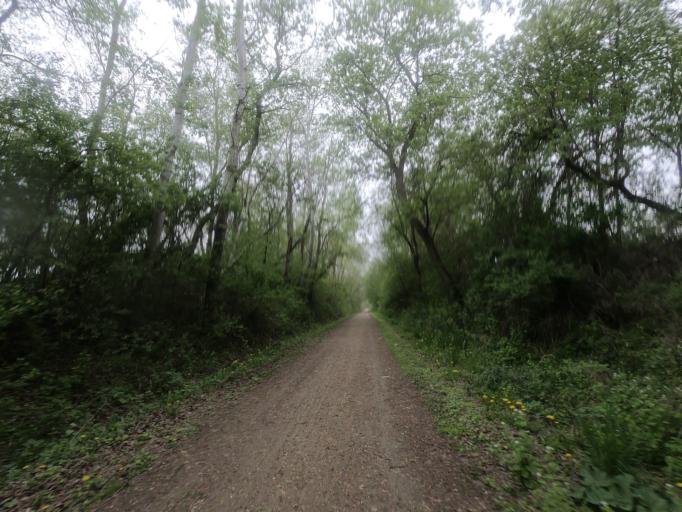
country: US
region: Wisconsin
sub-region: Jefferson County
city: Jefferson
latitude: 43.0367
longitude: -88.8166
